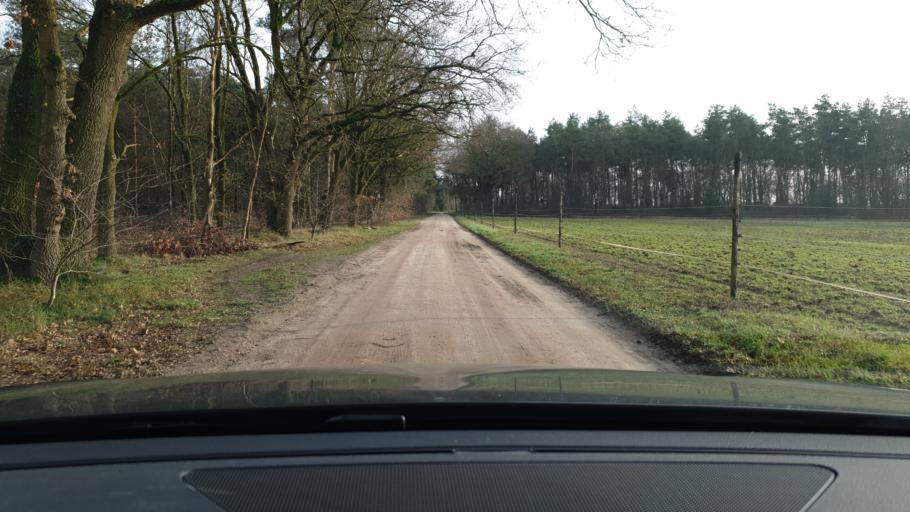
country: NL
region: Limburg
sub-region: Gemeente Peel en Maas
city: Maasbree
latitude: 51.4364
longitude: 6.0695
